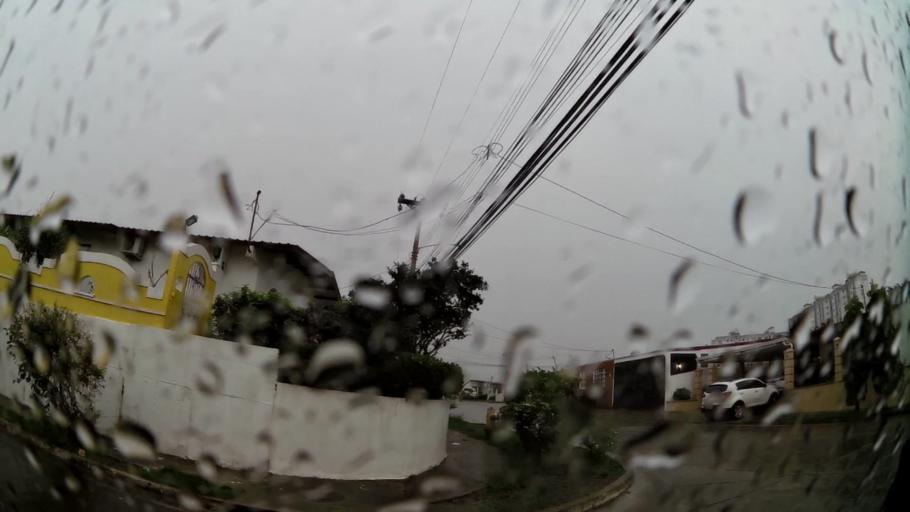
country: PA
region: Panama
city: San Miguelito
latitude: 9.0499
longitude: -79.4675
